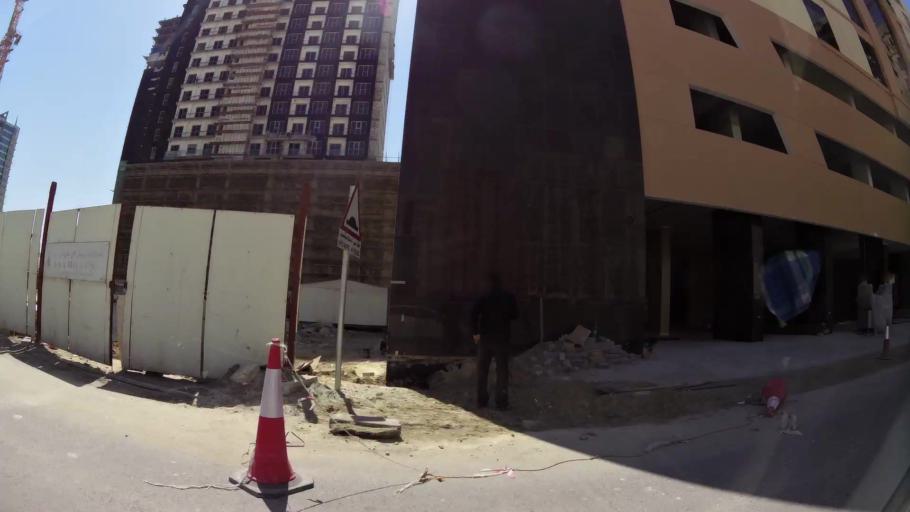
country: BH
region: Manama
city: Manama
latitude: 26.2201
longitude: 50.6093
